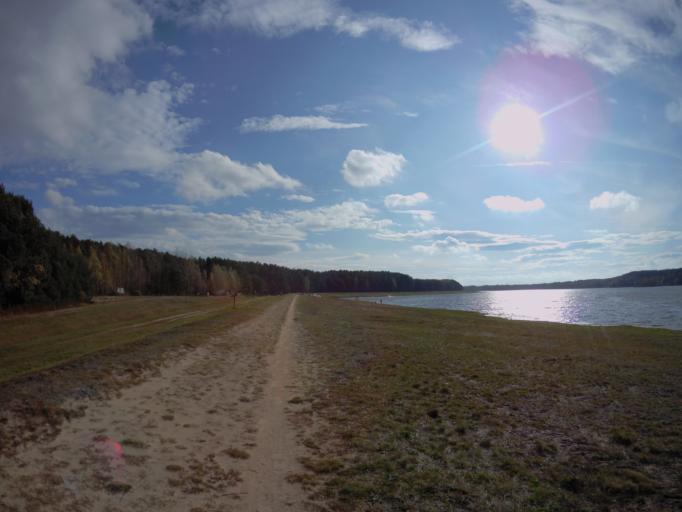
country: PL
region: Subcarpathian Voivodeship
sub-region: Powiat kolbuszowski
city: Lipnica
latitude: 50.3369
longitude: 21.9425
